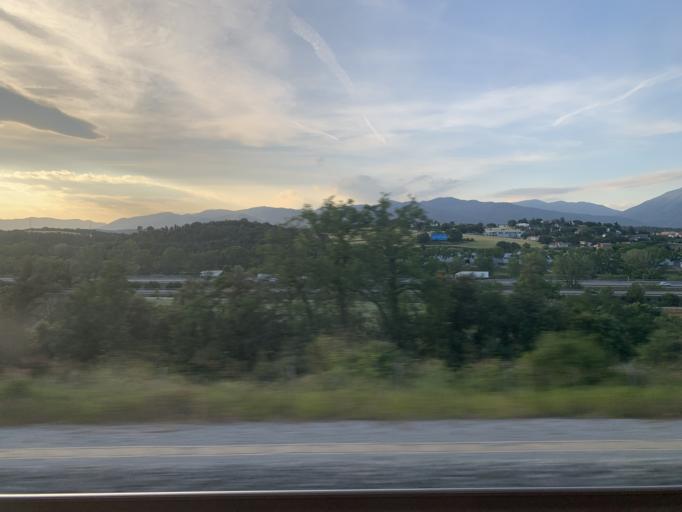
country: ES
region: Catalonia
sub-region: Provincia de Barcelona
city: Llinars del Valles
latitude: 41.6296
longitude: 2.3909
